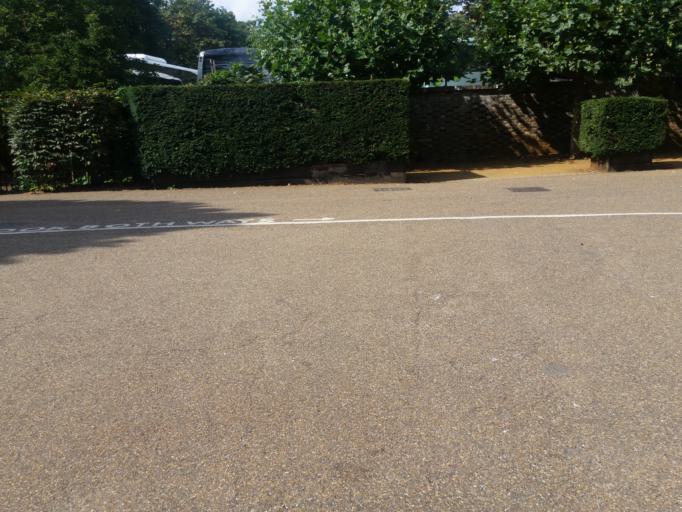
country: GB
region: England
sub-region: Greater London
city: Bayswater
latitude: 51.5097
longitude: -0.1895
